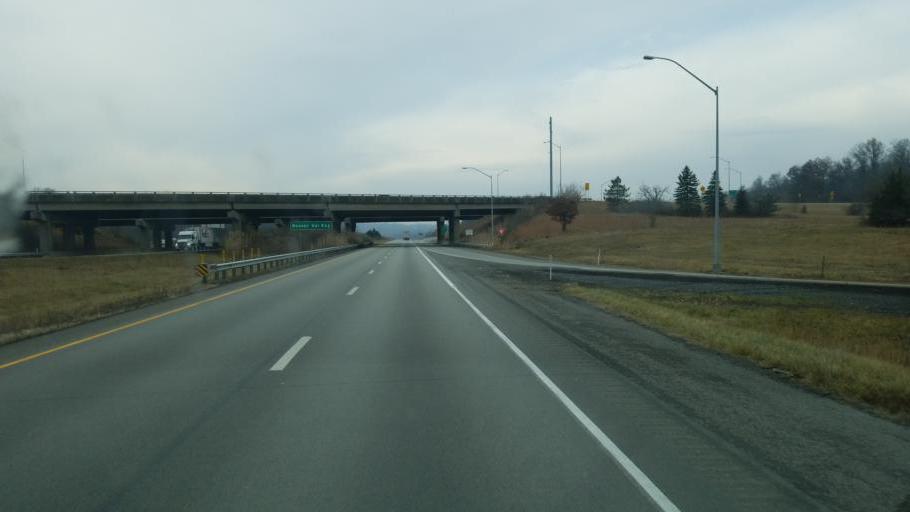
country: US
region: Pennsylvania
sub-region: Mercer County
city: Hermitage
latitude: 41.1850
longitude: -80.4420
